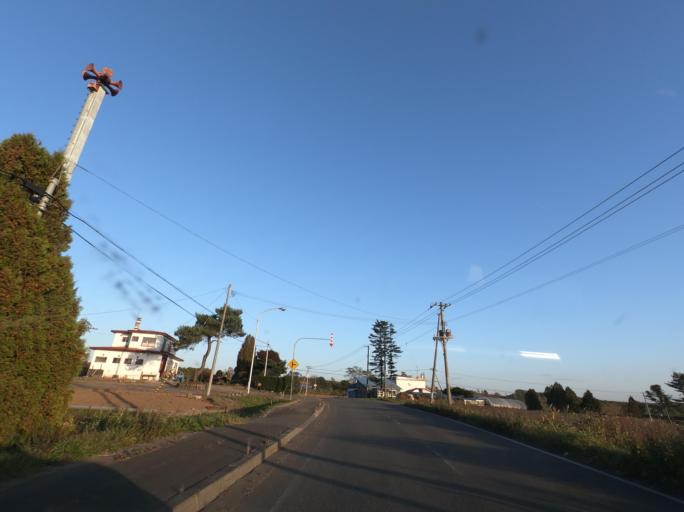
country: JP
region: Hokkaido
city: Chitose
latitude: 42.9282
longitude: 141.7680
